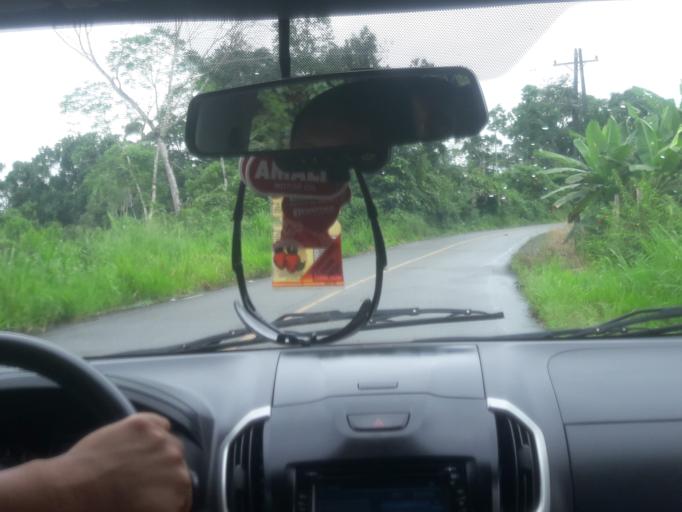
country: EC
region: Napo
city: Tena
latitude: -1.0373
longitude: -77.6910
